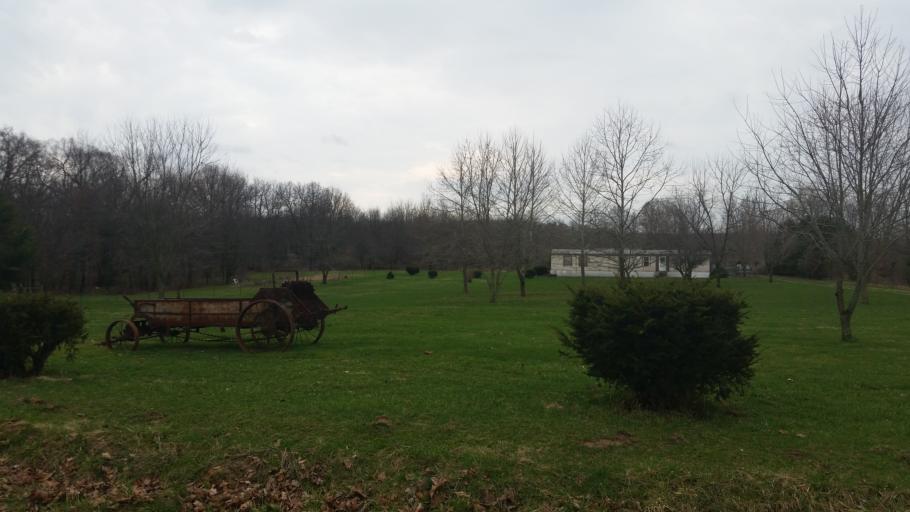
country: US
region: Ohio
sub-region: Knox County
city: Oak Hill
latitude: 40.2988
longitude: -82.2475
